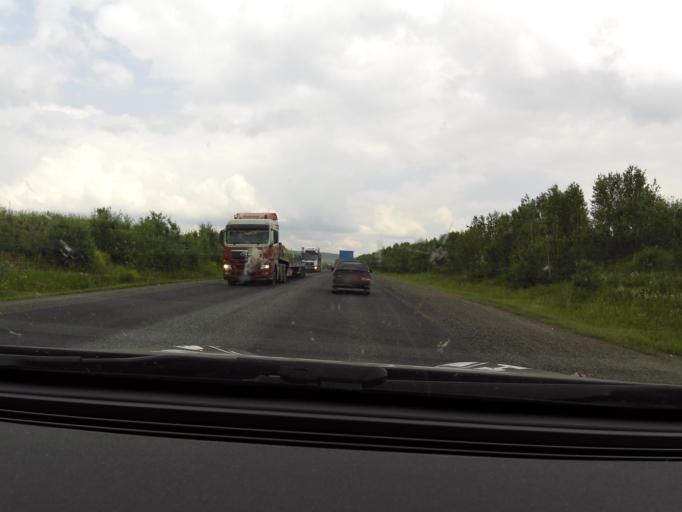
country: RU
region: Sverdlovsk
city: Ufimskiy
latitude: 56.7691
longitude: 58.2016
